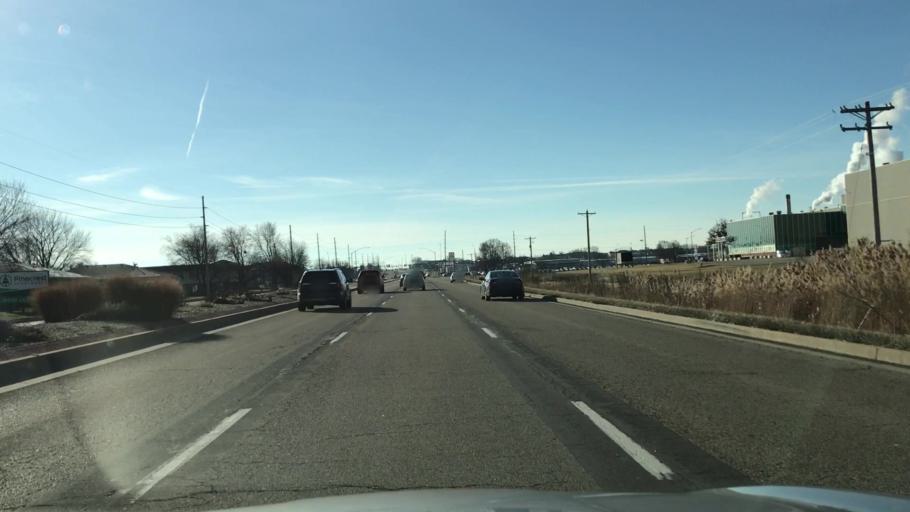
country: US
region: Illinois
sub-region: McLean County
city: Normal
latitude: 40.5216
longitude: -88.9526
